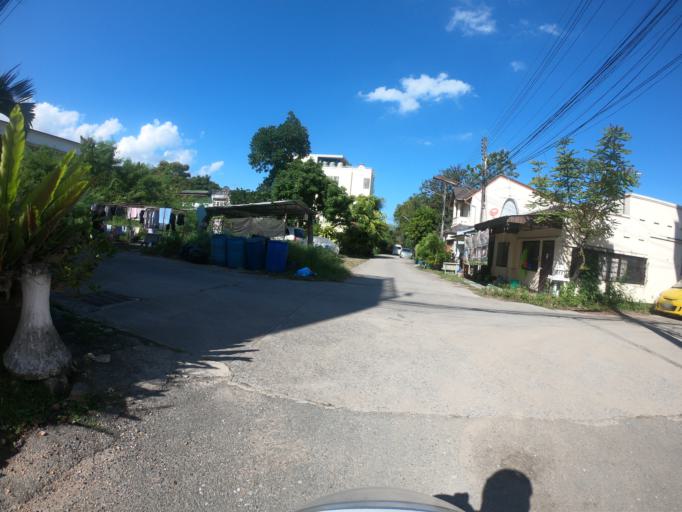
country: TH
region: Chiang Mai
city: Chiang Mai
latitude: 18.8020
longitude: 98.9740
